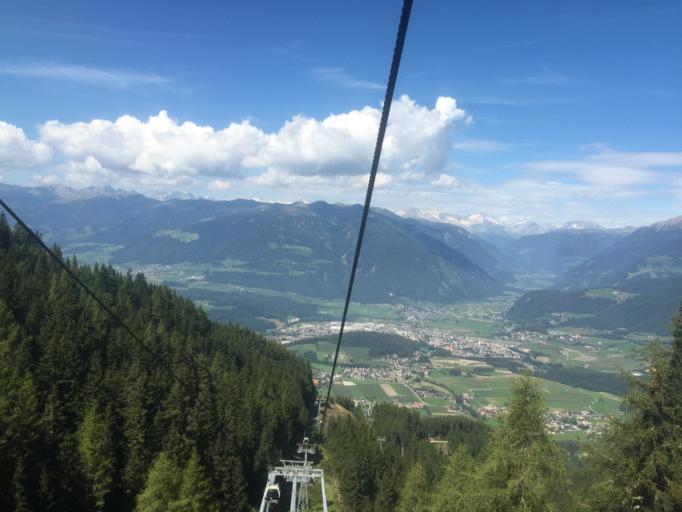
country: IT
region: Trentino-Alto Adige
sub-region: Bolzano
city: Riscone
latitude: 46.7518
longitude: 11.9508
